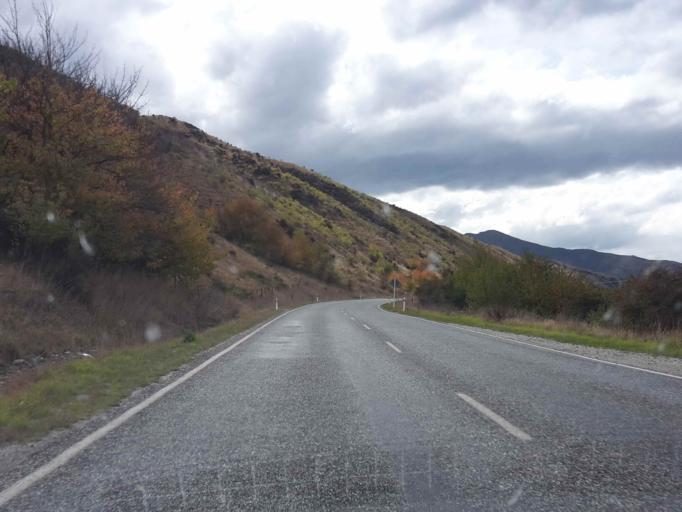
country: NZ
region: Otago
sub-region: Queenstown-Lakes District
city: Wanaka
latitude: -44.8198
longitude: 169.0625
